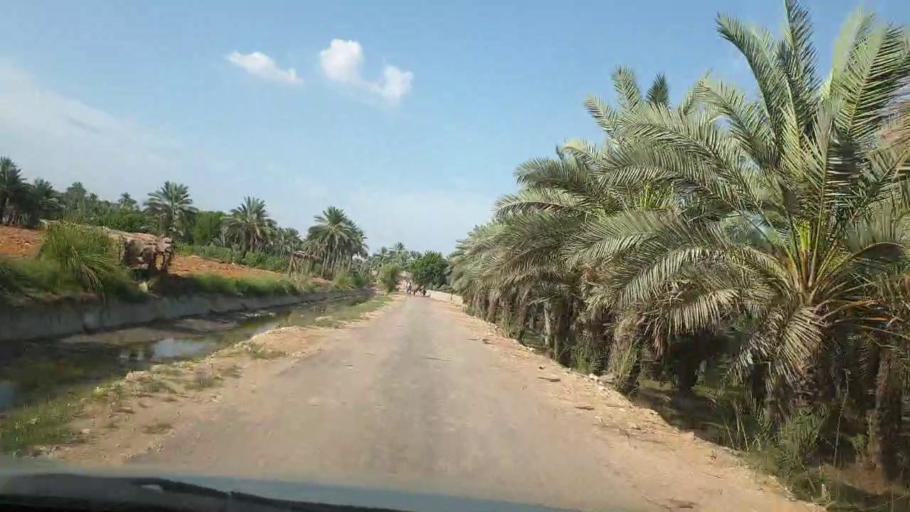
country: PK
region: Sindh
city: Sukkur
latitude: 27.6526
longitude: 68.8290
